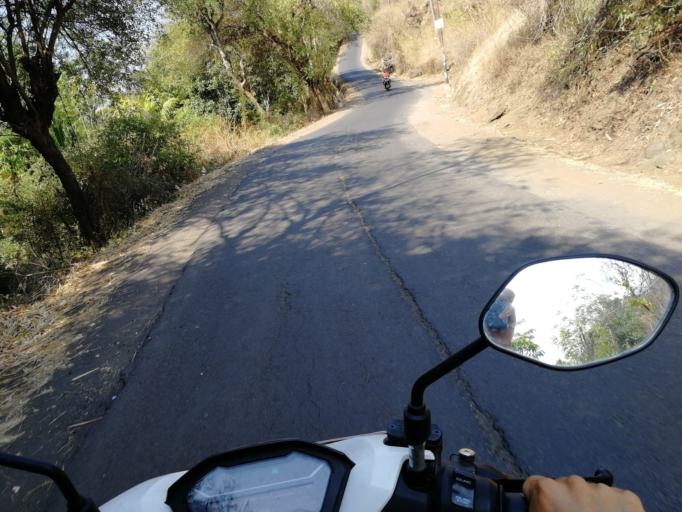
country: ID
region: Bali
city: Biaslantang Kaler
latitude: -8.3467
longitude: 115.6736
